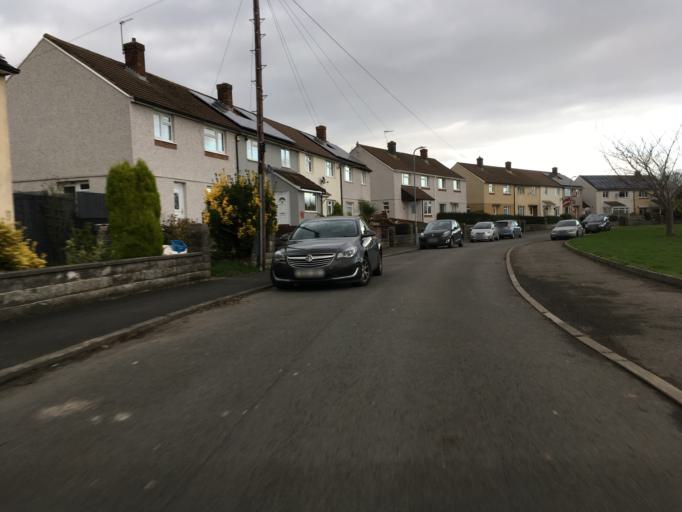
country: GB
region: Wales
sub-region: Monmouthshire
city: Chepstow
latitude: 51.6293
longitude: -2.6777
